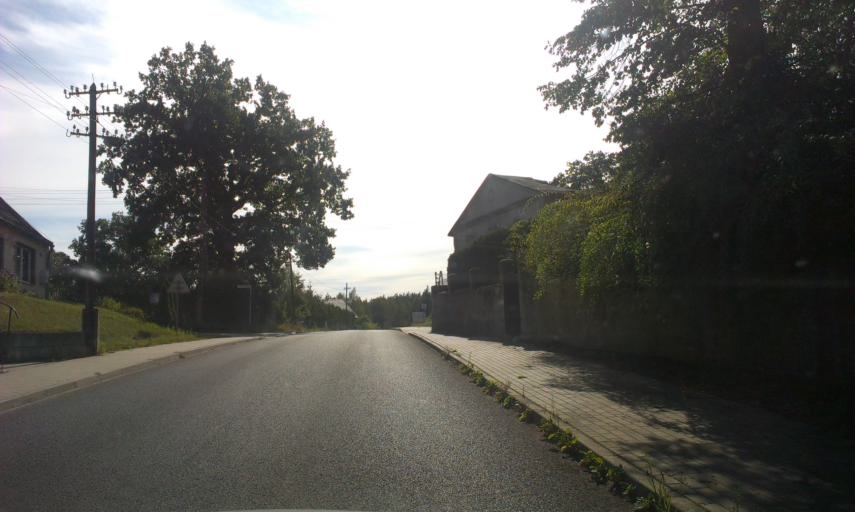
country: PL
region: Greater Poland Voivodeship
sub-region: Powiat zlotowski
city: Okonek
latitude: 53.5337
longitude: 16.9533
